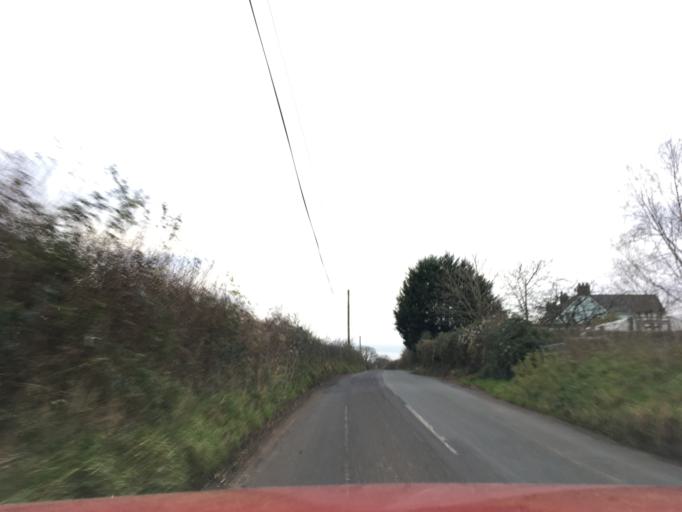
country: GB
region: Wales
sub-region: Monmouthshire
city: Caldicot
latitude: 51.6016
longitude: -2.7099
